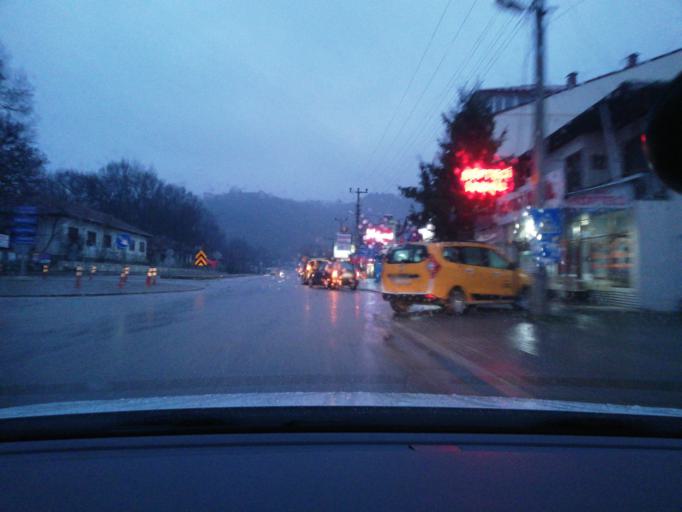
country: TR
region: Bolu
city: Bolu
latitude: 40.6900
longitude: 31.6199
